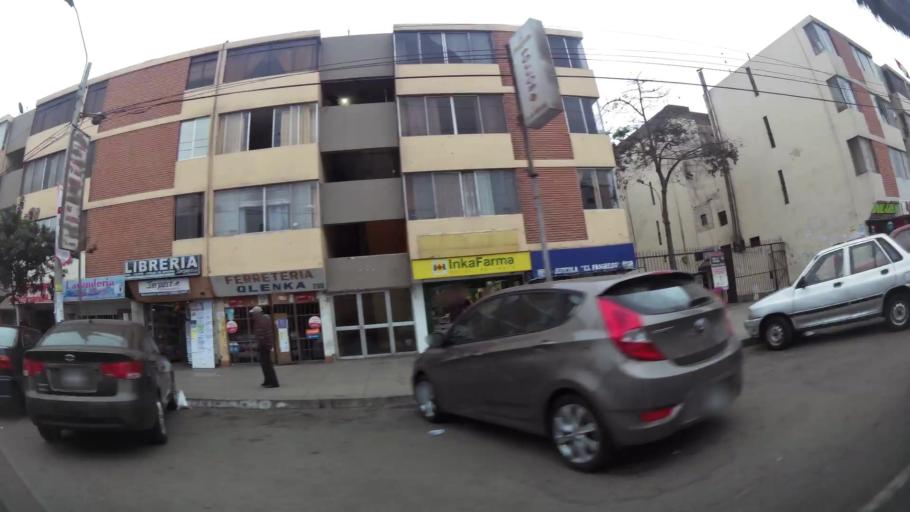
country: PE
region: Callao
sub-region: Callao
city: Callao
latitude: -12.0682
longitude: -77.1040
